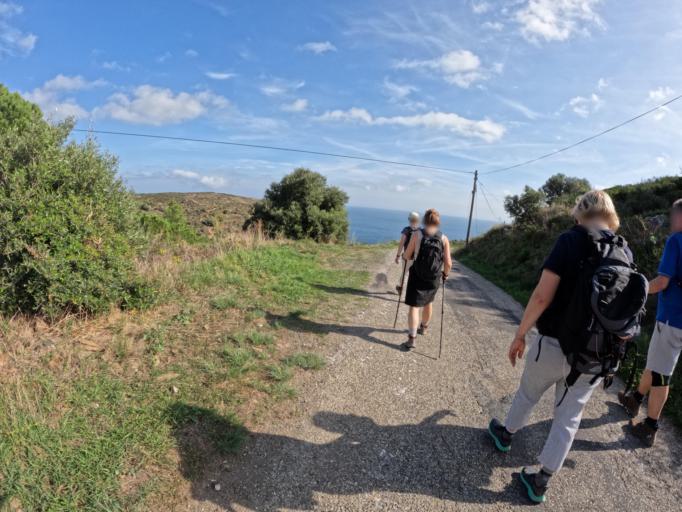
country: FR
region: Languedoc-Roussillon
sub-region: Departement des Pyrenees-Orientales
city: Cervera de la Marenda
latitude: 42.4641
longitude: 3.1563
